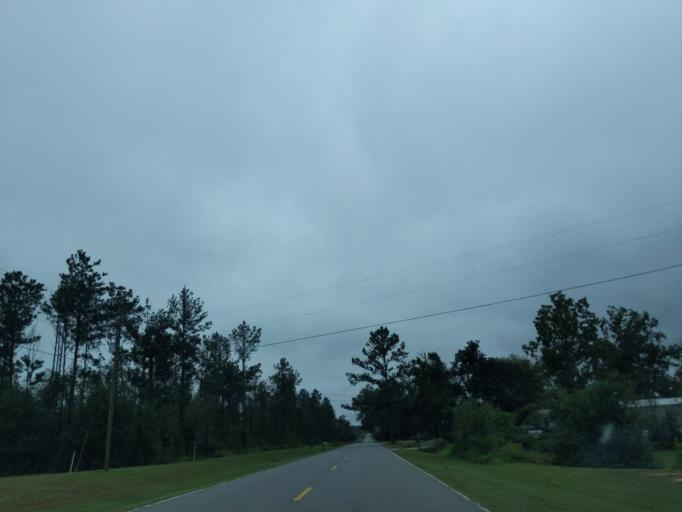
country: US
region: Florida
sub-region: Jackson County
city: Sneads
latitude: 30.7027
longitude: -84.9238
